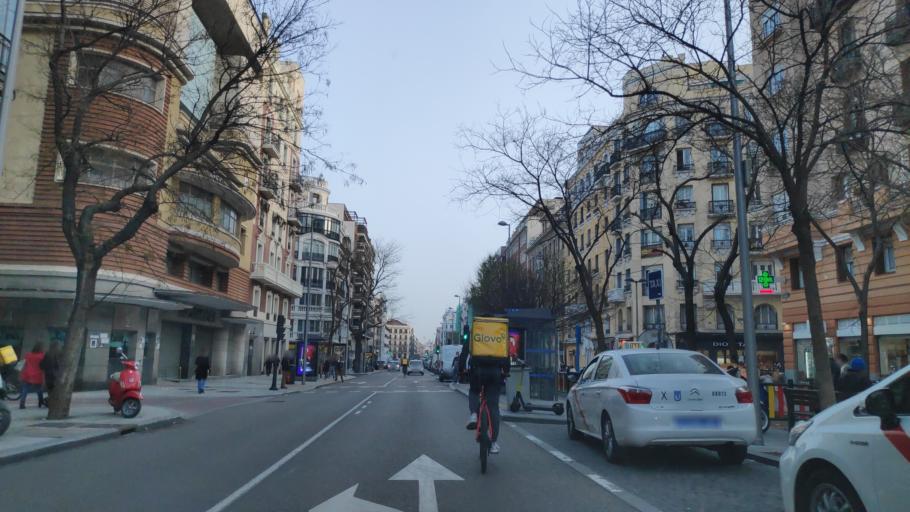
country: ES
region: Madrid
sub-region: Provincia de Madrid
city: Chamberi
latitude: 40.4318
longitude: -3.7036
